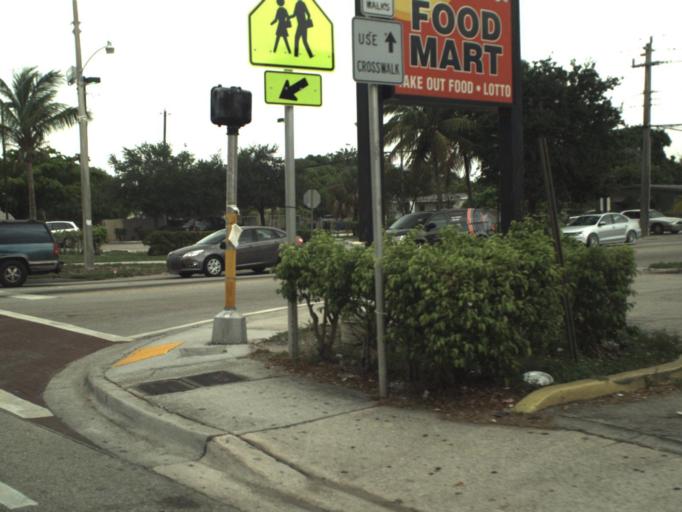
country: US
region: Florida
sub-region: Broward County
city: Roosevelt Gardens
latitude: 26.1367
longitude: -80.1619
